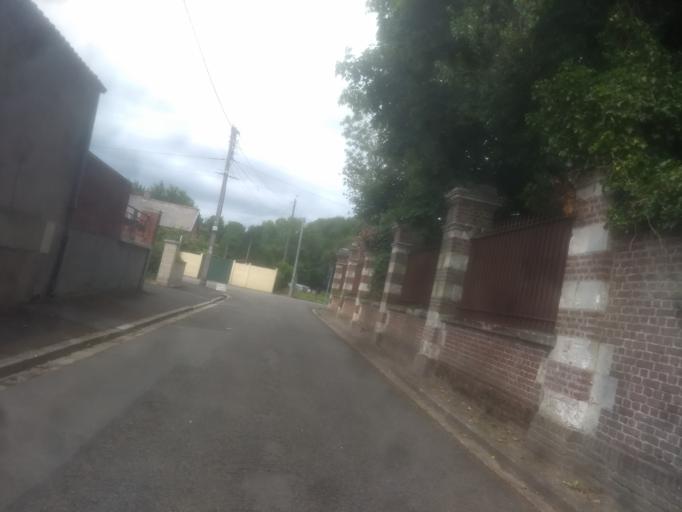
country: FR
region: Nord-Pas-de-Calais
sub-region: Departement du Pas-de-Calais
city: Maroeuil
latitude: 50.3225
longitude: 2.7031
